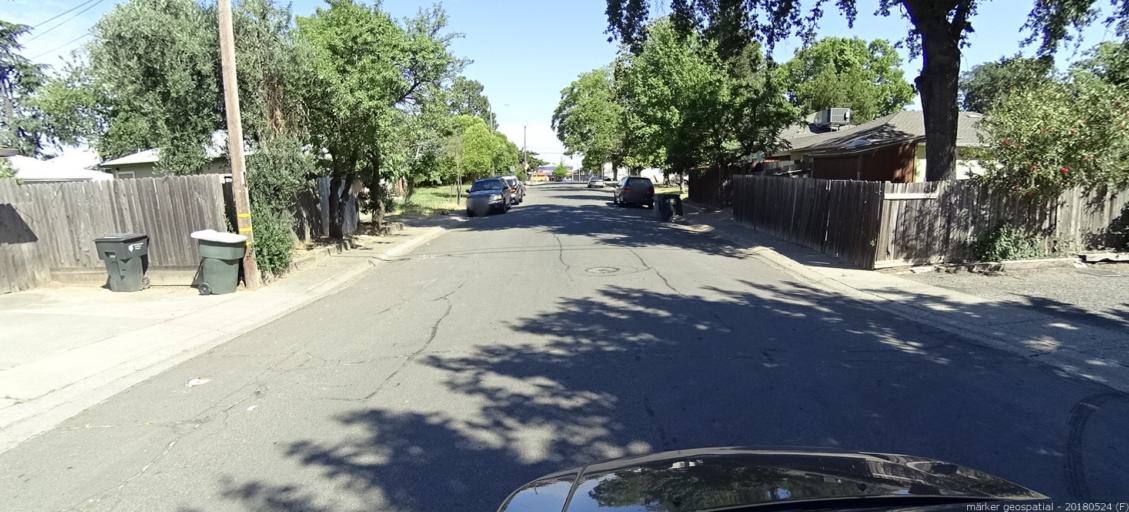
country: US
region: California
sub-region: Sacramento County
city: Sacramento
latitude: 38.6022
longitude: -121.4634
